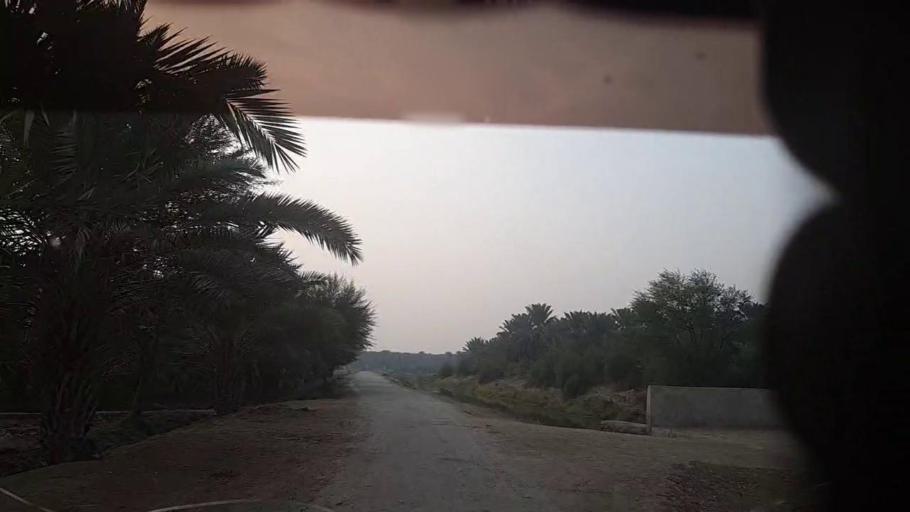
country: PK
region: Sindh
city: Pir jo Goth
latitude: 27.5215
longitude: 68.6458
